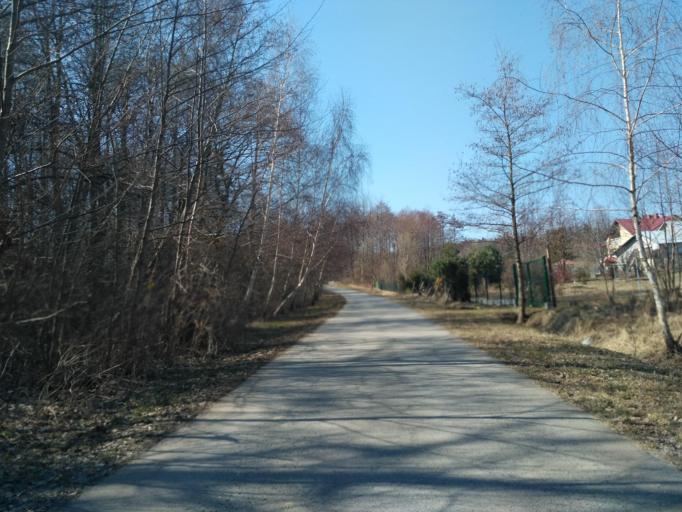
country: PL
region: Subcarpathian Voivodeship
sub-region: Powiat rzeszowski
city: Niechobrz
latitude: 49.9706
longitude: 21.8793
